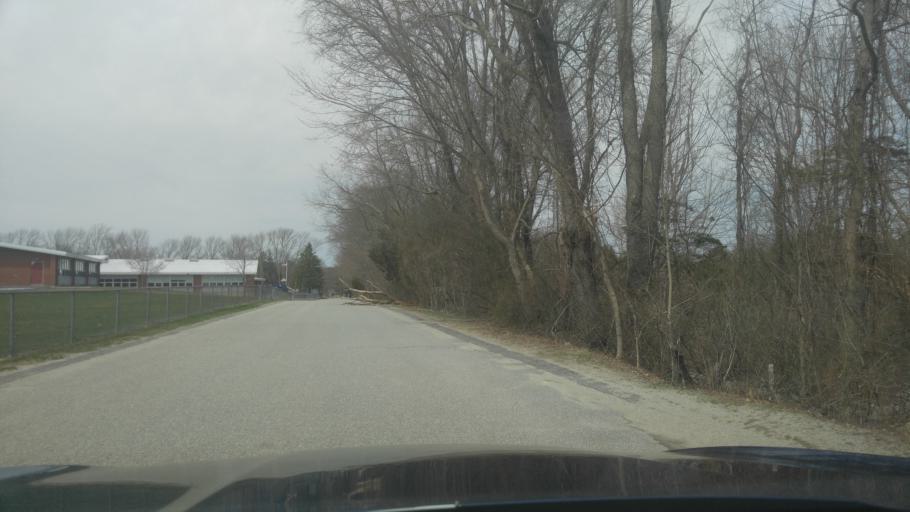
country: US
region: Rhode Island
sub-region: Washington County
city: Exeter
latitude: 41.6239
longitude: -71.5040
